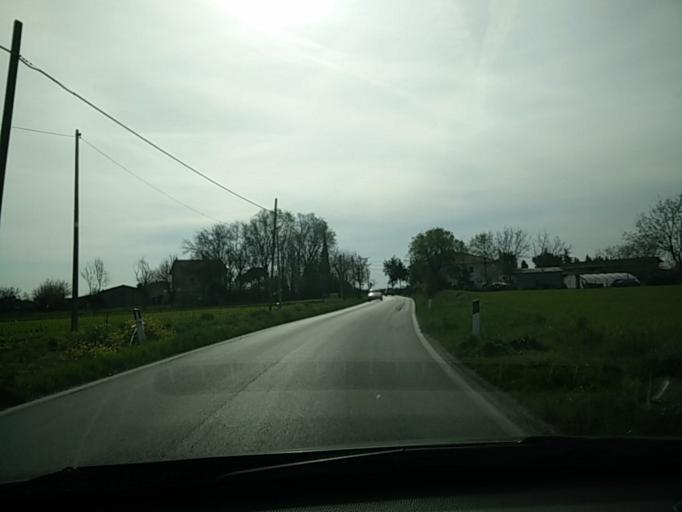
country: IT
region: Emilia-Romagna
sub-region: Provincia di Rimini
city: Santa Giustina
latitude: 44.0822
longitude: 12.4944
